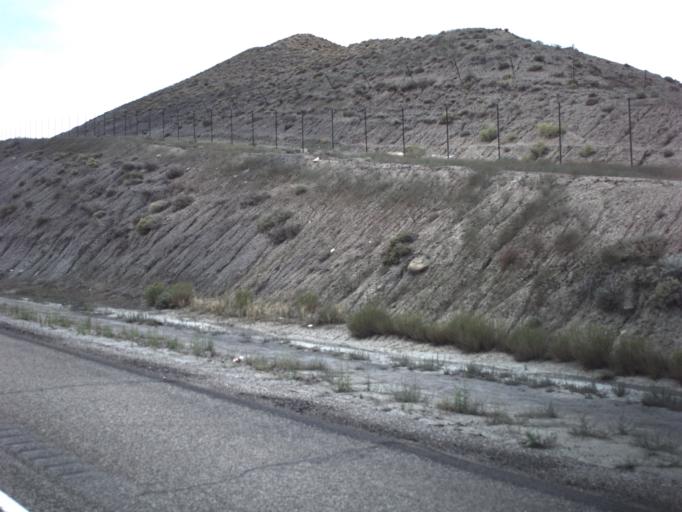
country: US
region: Utah
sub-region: Carbon County
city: Carbonville
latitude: 39.6215
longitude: -110.8569
